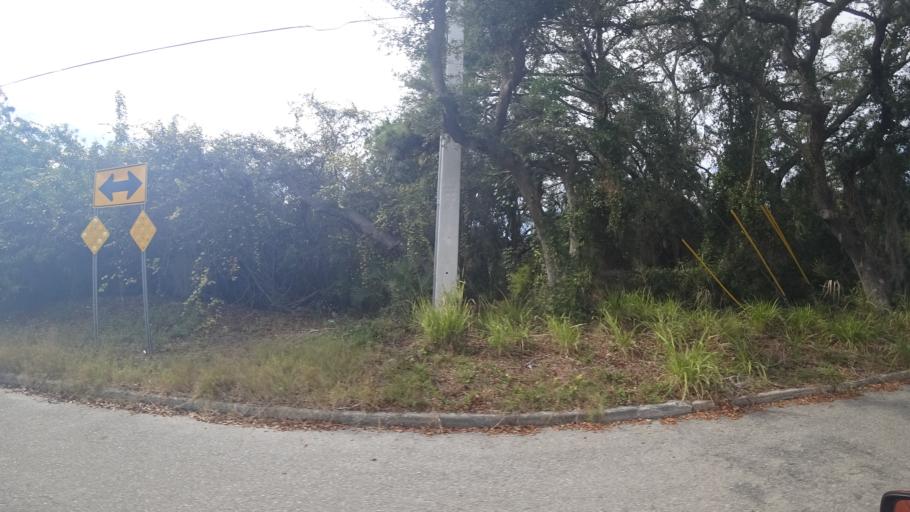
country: US
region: Florida
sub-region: Manatee County
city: West Bradenton
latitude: 27.4998
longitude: -82.6409
